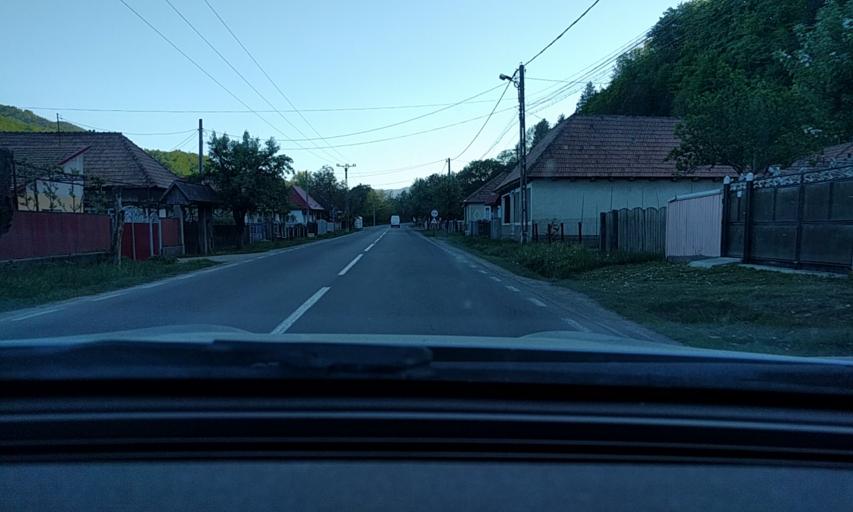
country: RO
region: Bacau
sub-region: Oras Slanic-Moldova
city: Slanic-Moldova
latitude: 46.1768
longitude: 26.4803
